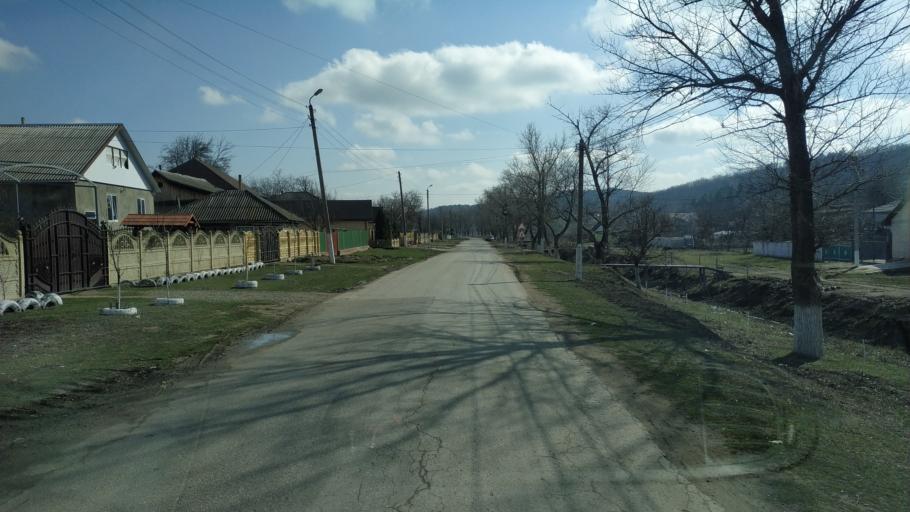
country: MD
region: Hincesti
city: Hincesti
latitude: 46.8765
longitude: 28.6290
